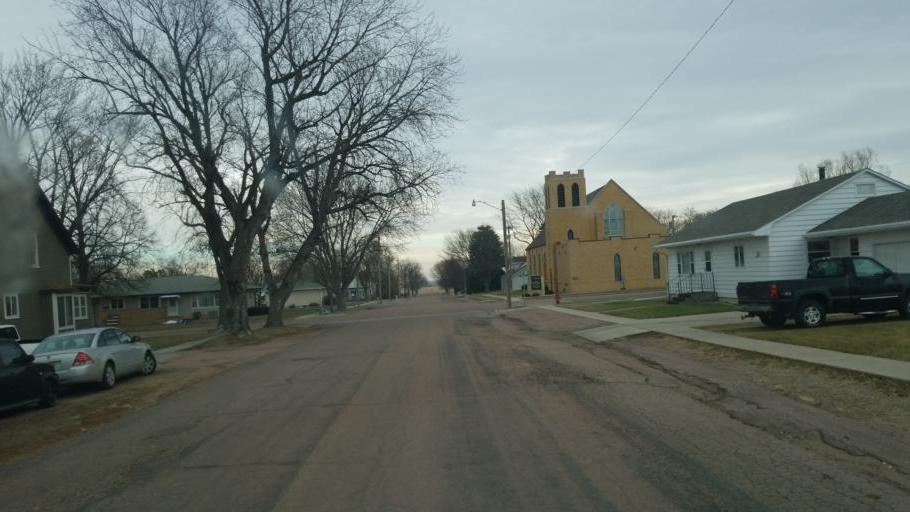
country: US
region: South Dakota
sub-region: Hutchinson County
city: Parkston
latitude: 43.2245
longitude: -97.9635
